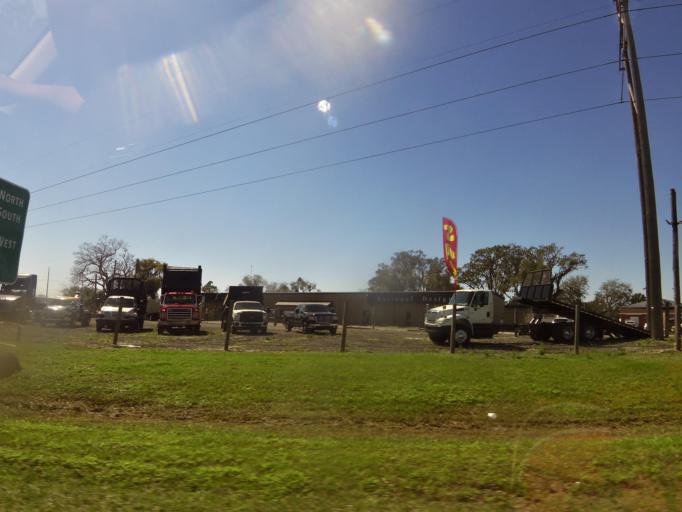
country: US
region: Florida
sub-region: Orange County
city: Lockhart
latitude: 28.6382
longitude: -81.4554
